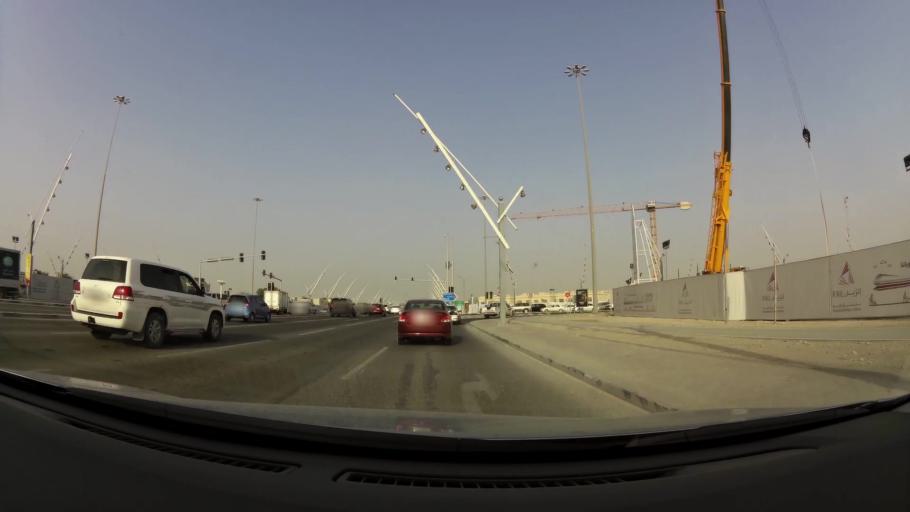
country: QA
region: Baladiyat ar Rayyan
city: Ar Rayyan
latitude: 25.2606
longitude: 51.4537
